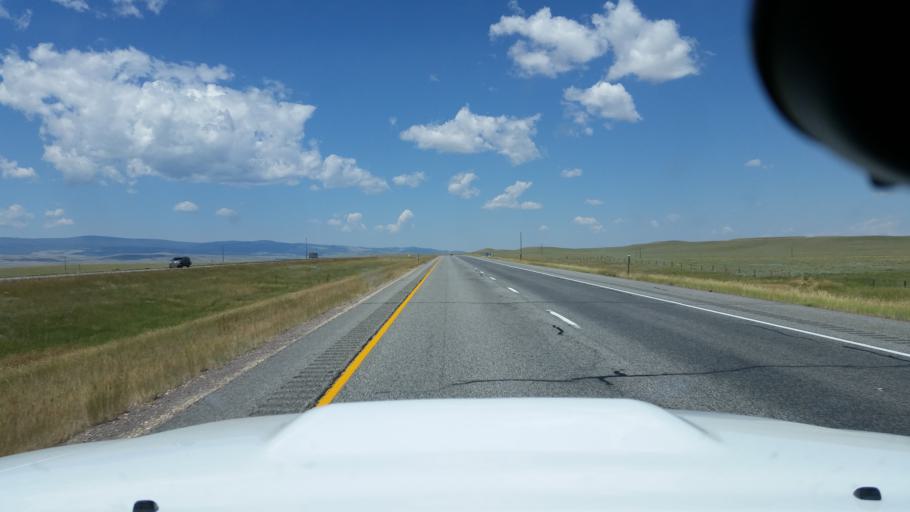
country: US
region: Wyoming
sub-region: Albany County
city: Laramie
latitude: 41.4282
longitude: -105.8804
